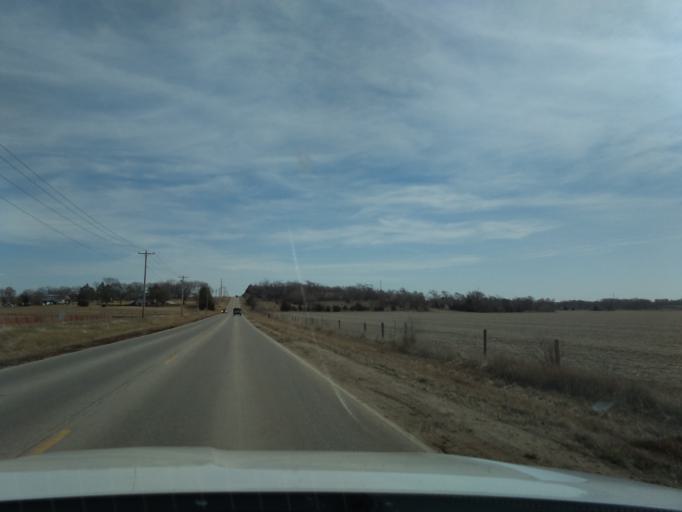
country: US
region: Nebraska
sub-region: Lancaster County
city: Hickman
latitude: 40.6973
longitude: -96.6788
